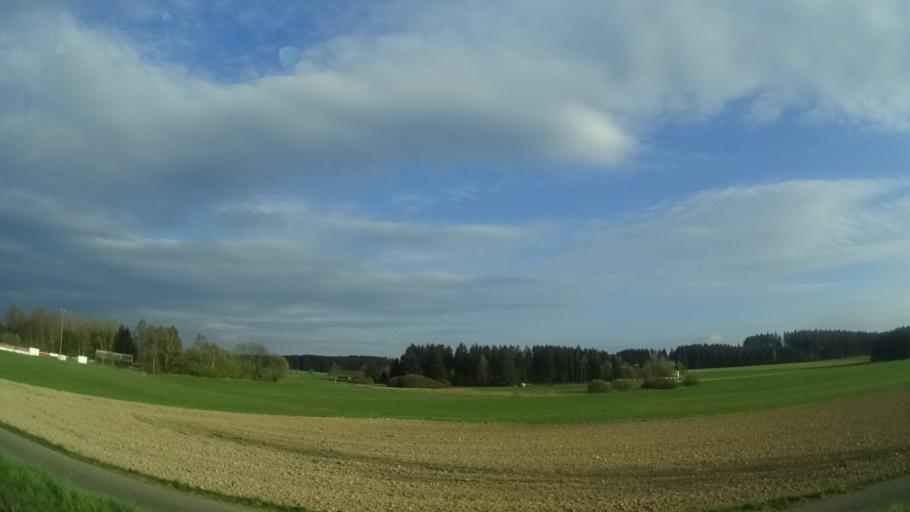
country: DE
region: Bavaria
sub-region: Upper Franconia
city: Koditz
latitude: 50.3027
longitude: 11.8439
